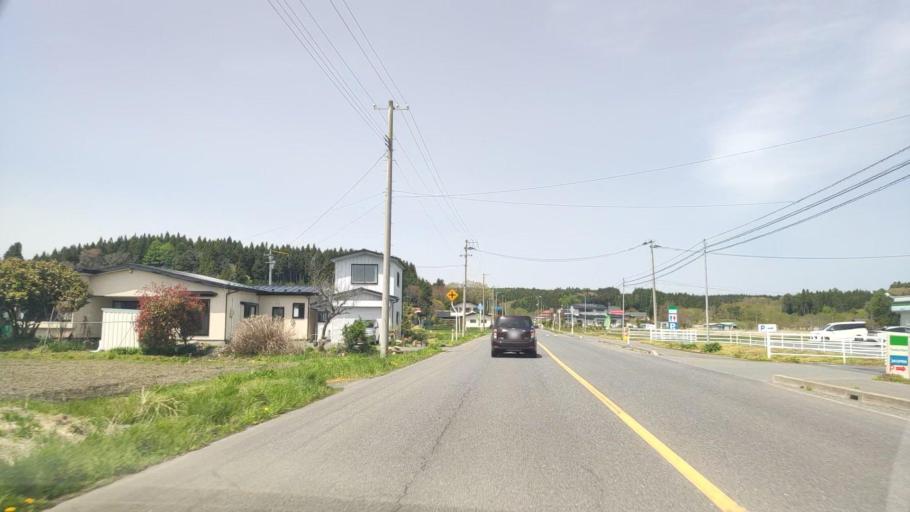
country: JP
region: Aomori
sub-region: Misawa Shi
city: Inuotose
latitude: 40.5591
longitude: 141.3862
